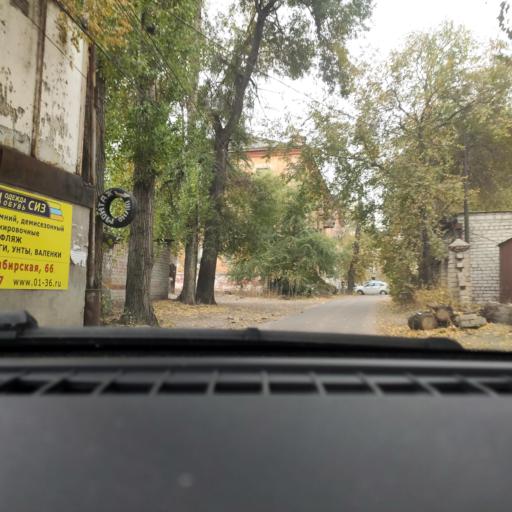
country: RU
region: Voronezj
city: Maslovka
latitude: 51.6216
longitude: 39.2453
